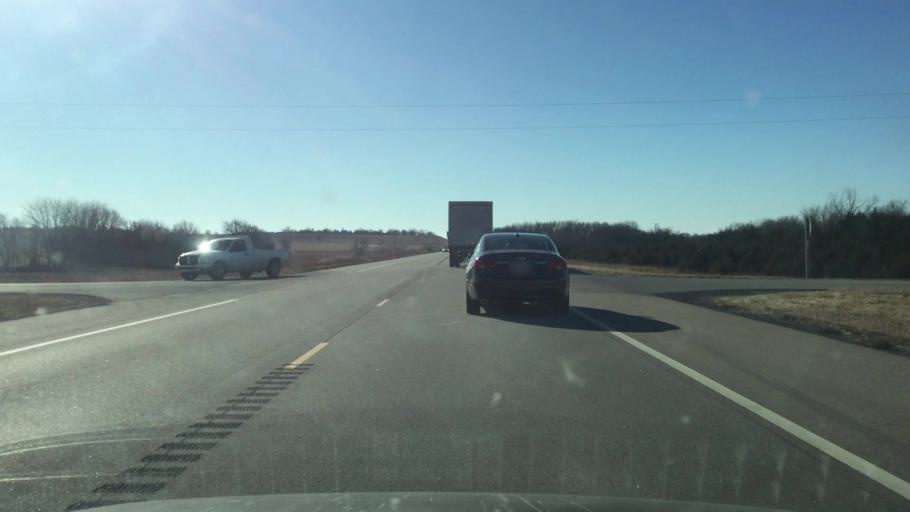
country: US
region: Kansas
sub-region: Allen County
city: Iola
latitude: 38.0241
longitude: -95.3807
